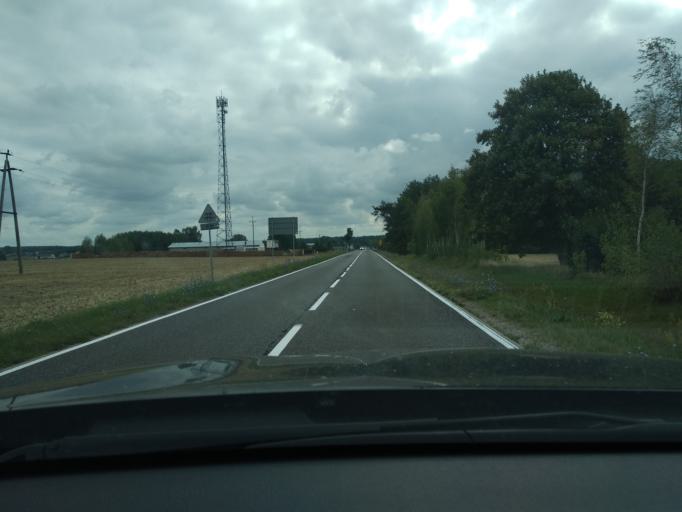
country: PL
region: Masovian Voivodeship
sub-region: Powiat pultuski
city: Obryte
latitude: 52.6519
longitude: 21.2393
